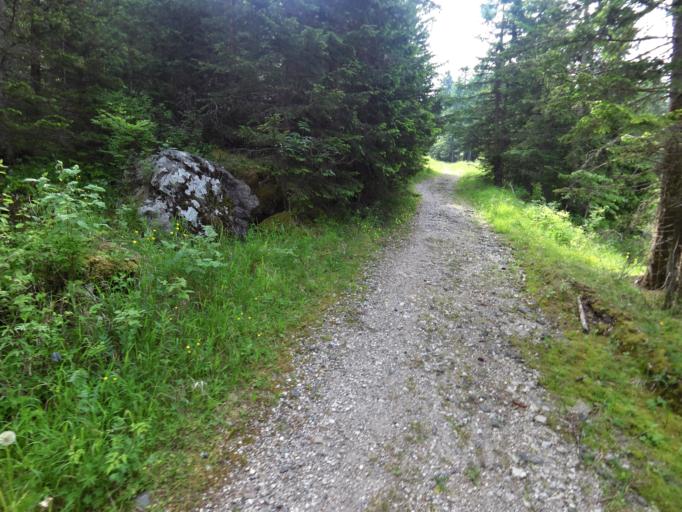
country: IT
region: Trentino-Alto Adige
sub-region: Bolzano
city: Siusi
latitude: 46.5417
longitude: 11.5922
